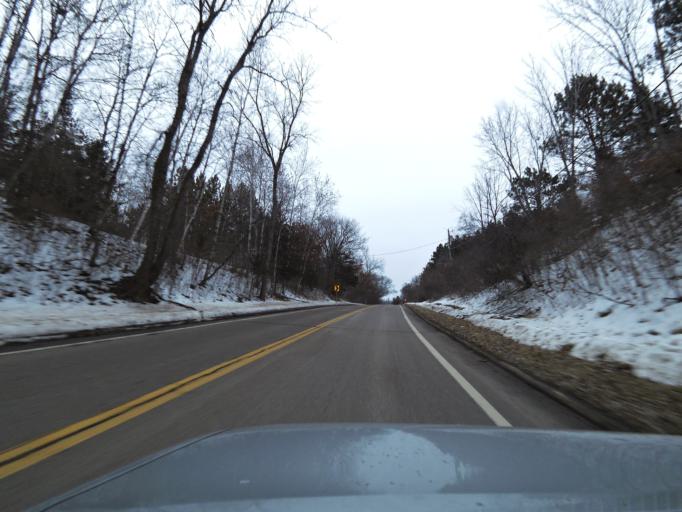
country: US
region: Minnesota
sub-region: Washington County
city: Afton
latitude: 44.8663
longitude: -92.8016
